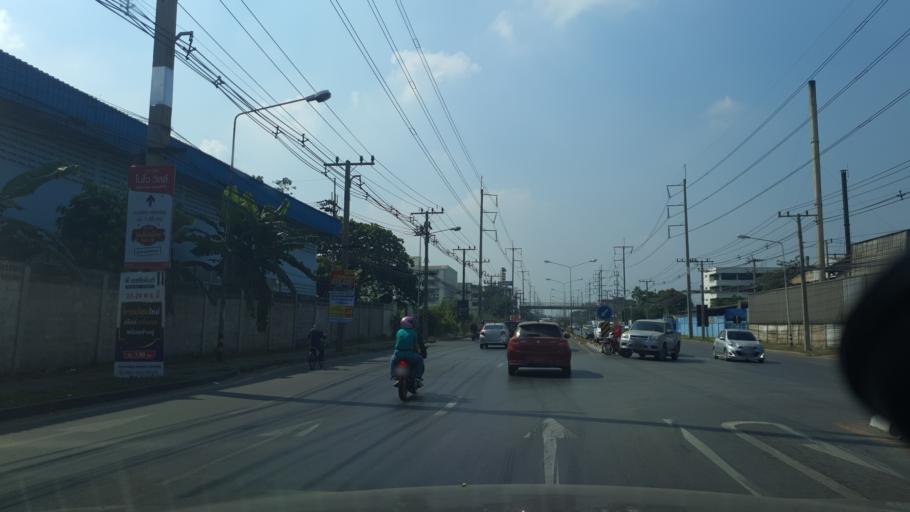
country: TH
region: Samut Sakhon
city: Krathum Baen
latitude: 13.6685
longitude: 100.2793
